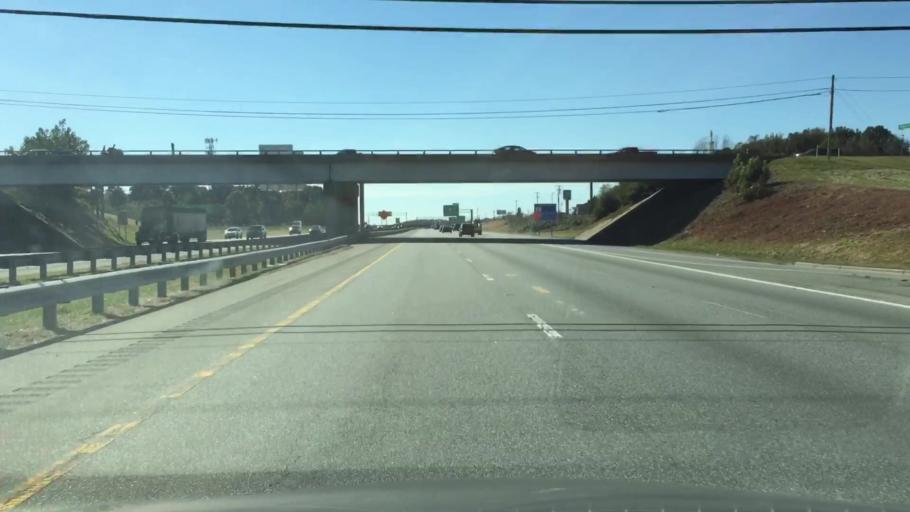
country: US
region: North Carolina
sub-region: Guilford County
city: Greensboro
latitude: 36.0116
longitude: -79.8390
